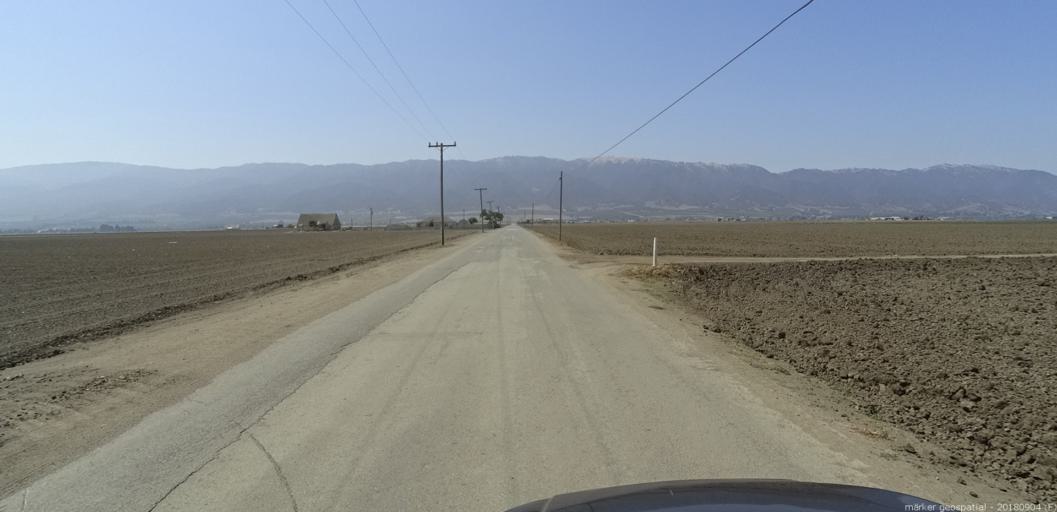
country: US
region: California
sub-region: Monterey County
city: Gonzales
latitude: 36.5134
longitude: -121.4674
